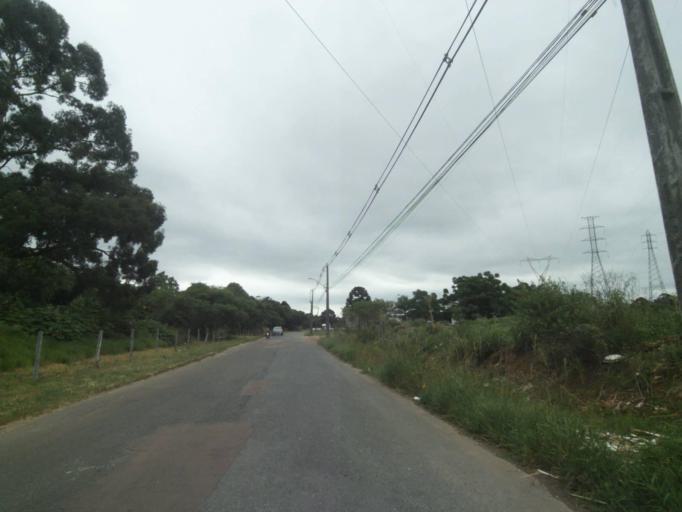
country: BR
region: Parana
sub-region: Araucaria
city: Araucaria
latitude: -25.5400
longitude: -49.3226
